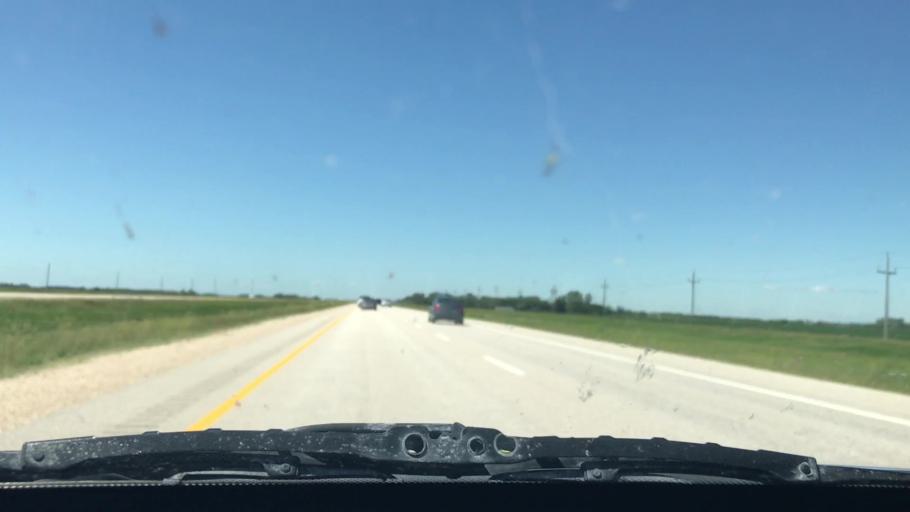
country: CA
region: Manitoba
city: Steinbach
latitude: 49.7370
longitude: -96.7355
